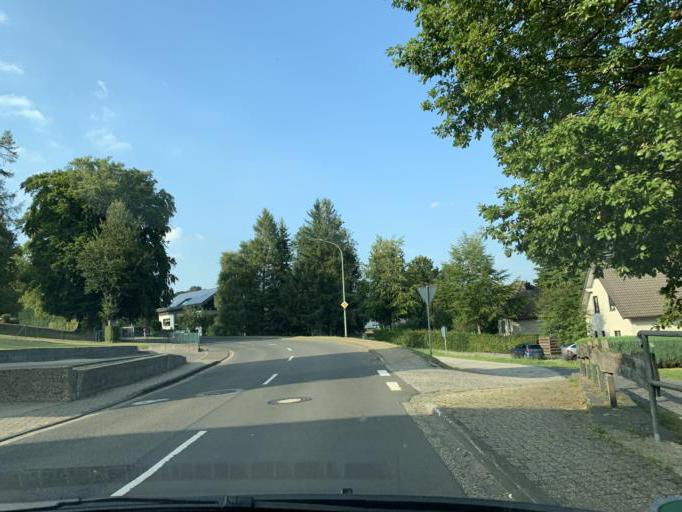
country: DE
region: North Rhine-Westphalia
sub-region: Regierungsbezirk Koln
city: Simmerath
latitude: 50.6248
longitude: 6.3553
